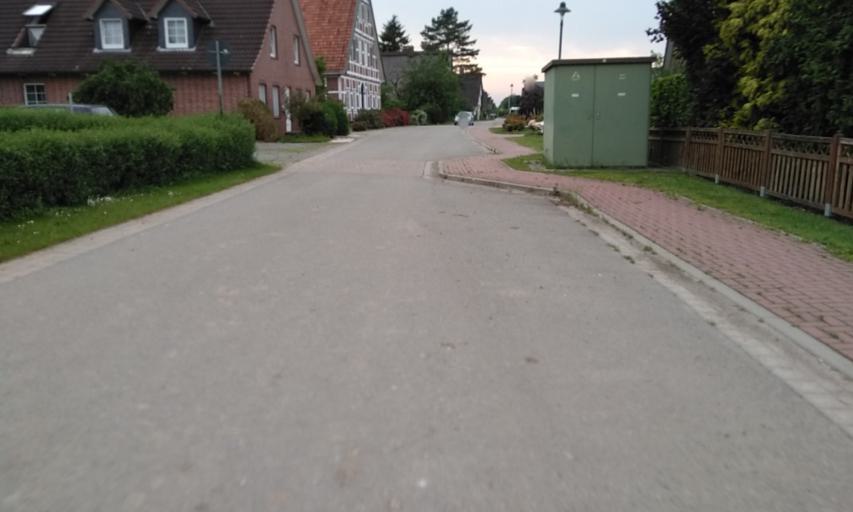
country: DE
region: Lower Saxony
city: Jork
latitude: 53.5132
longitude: 9.6926
